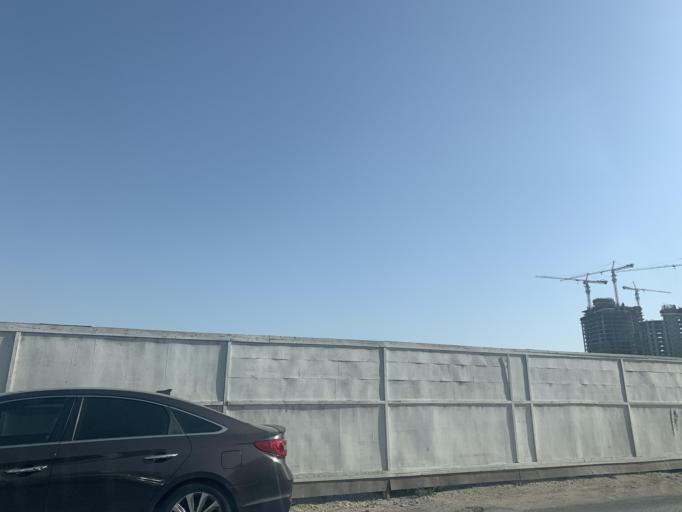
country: BH
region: Manama
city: Jidd Hafs
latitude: 26.2060
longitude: 50.4559
